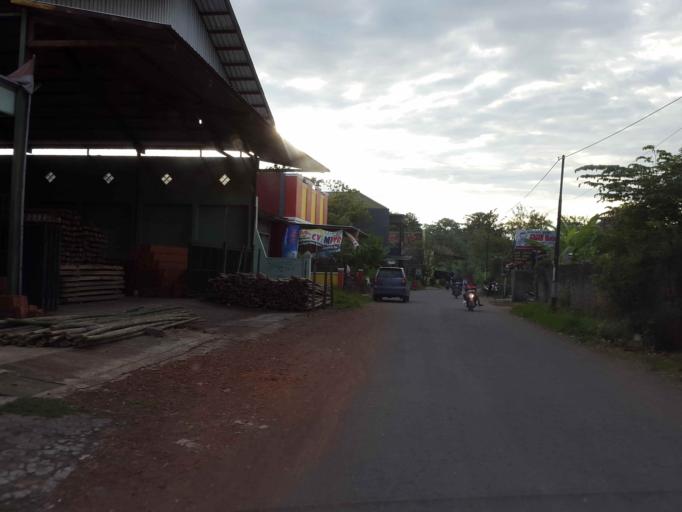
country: ID
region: Central Java
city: Ketanggungan
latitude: -6.9324
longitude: 108.8919
